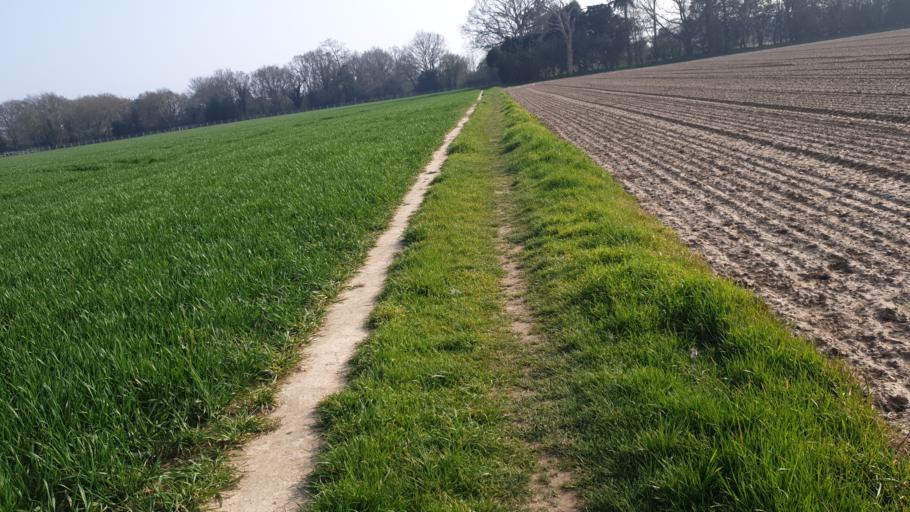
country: GB
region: England
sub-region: Essex
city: Little Clacton
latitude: 51.8781
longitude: 1.1180
